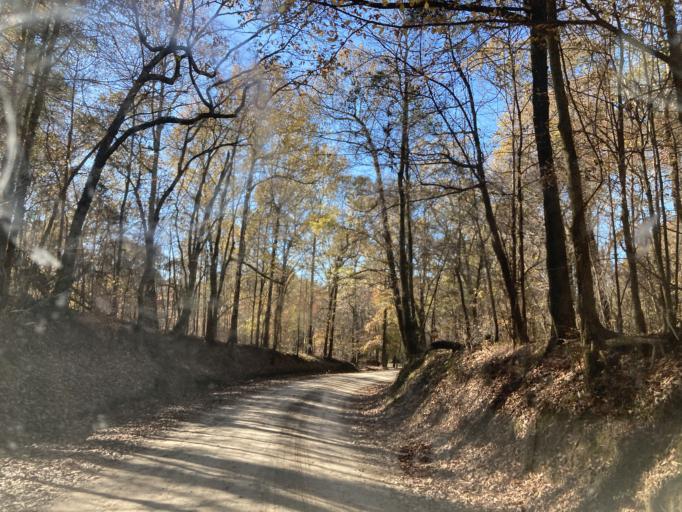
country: US
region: Mississippi
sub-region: Madison County
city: Kearney Park
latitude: 32.6699
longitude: -90.5094
